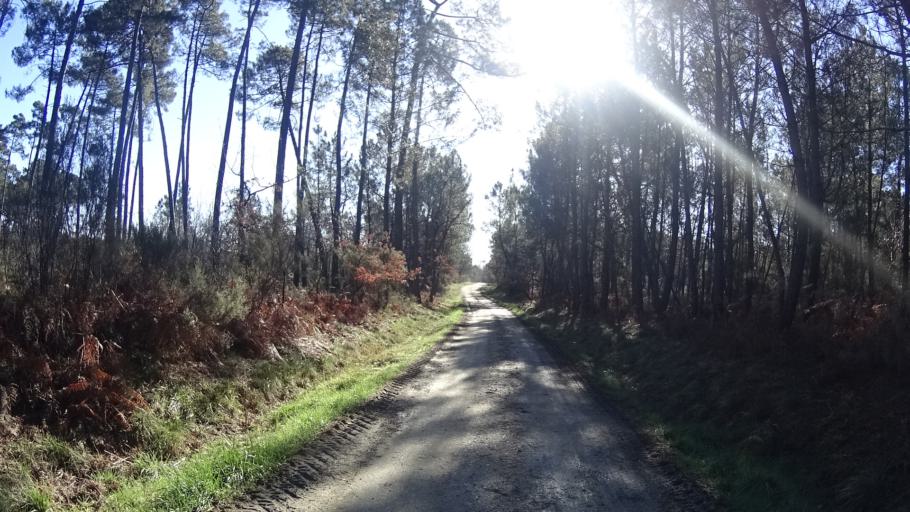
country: FR
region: Aquitaine
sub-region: Departement de la Dordogne
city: La Roche-Chalais
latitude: 45.1681
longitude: 0.0392
